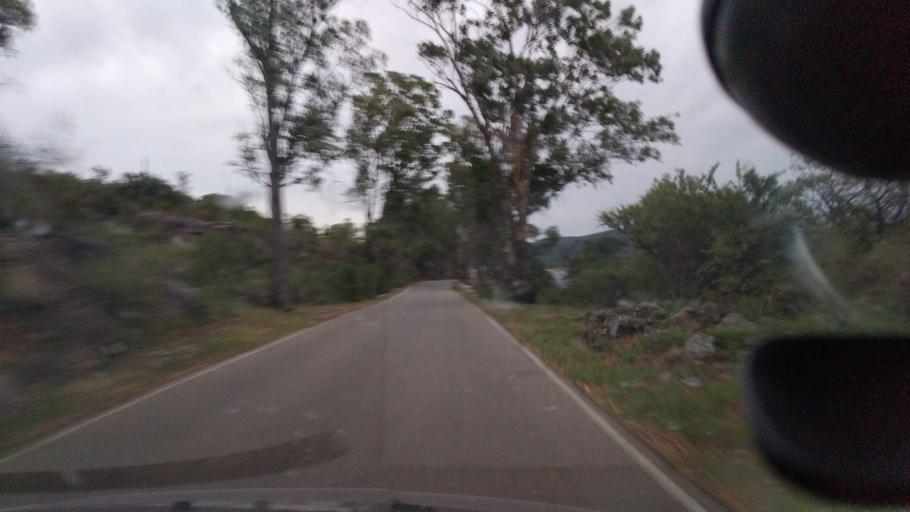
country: AR
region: Cordoba
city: Villa Las Rosas
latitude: -31.8773
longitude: -65.0288
